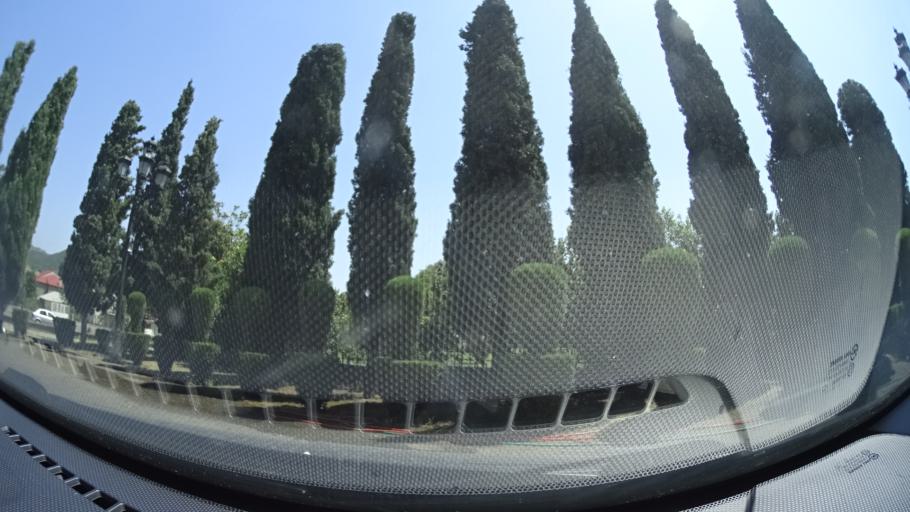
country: GE
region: Mtskheta-Mtianeti
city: Mtskheta
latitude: 41.8488
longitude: 44.7195
